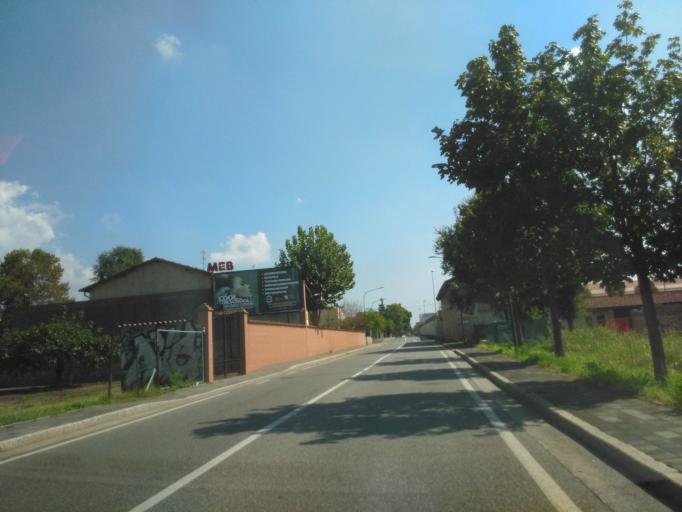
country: IT
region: Lombardy
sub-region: Provincia di Brescia
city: Brescia
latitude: 45.5411
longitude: 10.1876
